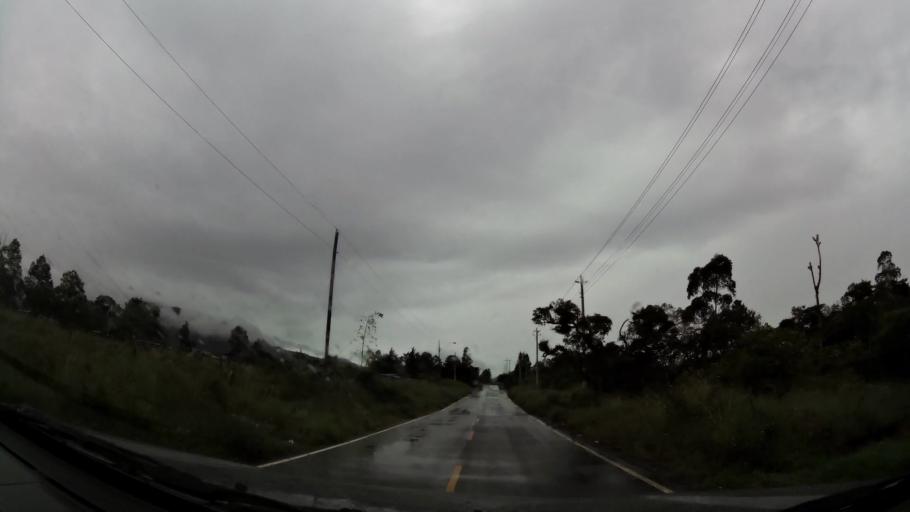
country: PA
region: Chiriqui
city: Volcan
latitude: 8.7970
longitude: -82.6476
